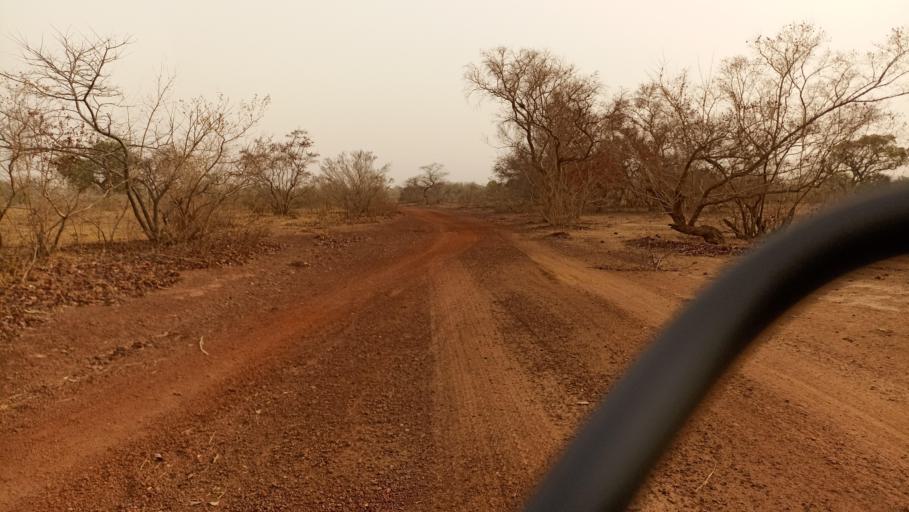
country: BF
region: Nord
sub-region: Province du Zondoma
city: Gourcy
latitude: 13.1540
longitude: -2.5950
